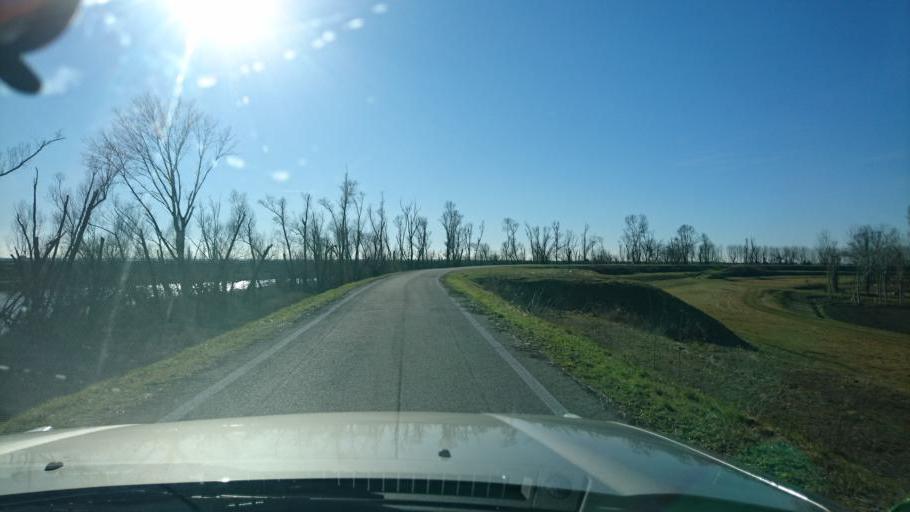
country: IT
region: Veneto
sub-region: Provincia di Rovigo
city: Ariano
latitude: 44.9295
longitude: 12.1450
